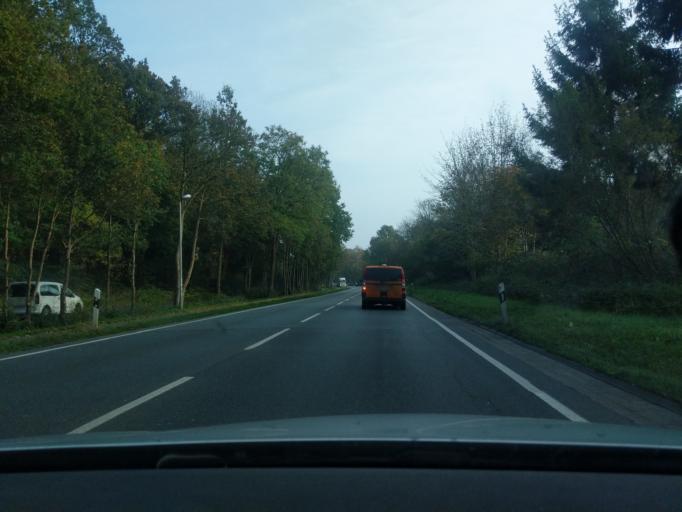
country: DE
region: Lower Saxony
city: Stade
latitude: 53.5924
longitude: 9.4423
